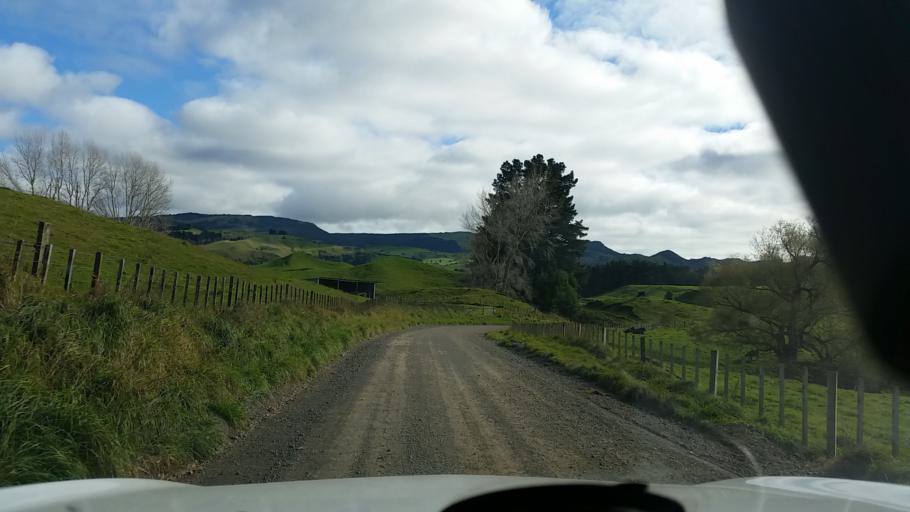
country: NZ
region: Hawke's Bay
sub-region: Napier City
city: Napier
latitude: -39.1083
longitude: 176.8917
